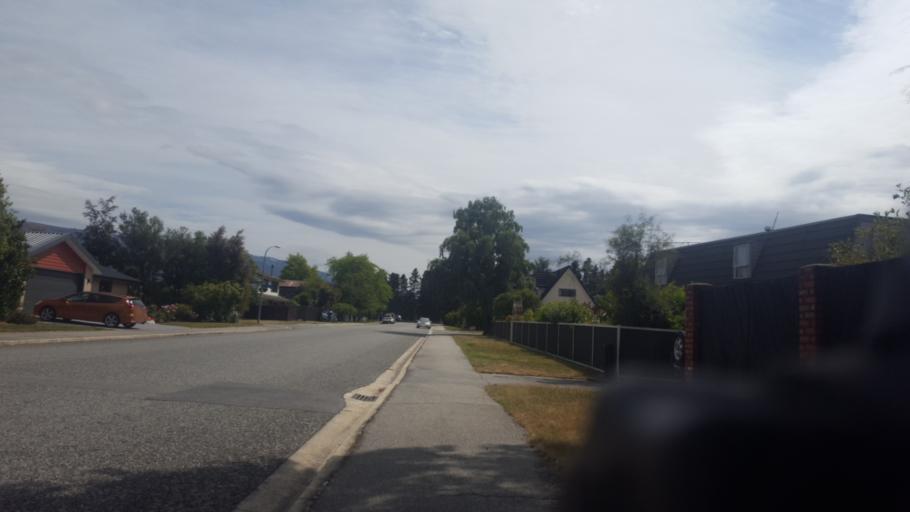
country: NZ
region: Otago
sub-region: Queenstown-Lakes District
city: Wanaka
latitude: -45.0416
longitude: 169.2017
